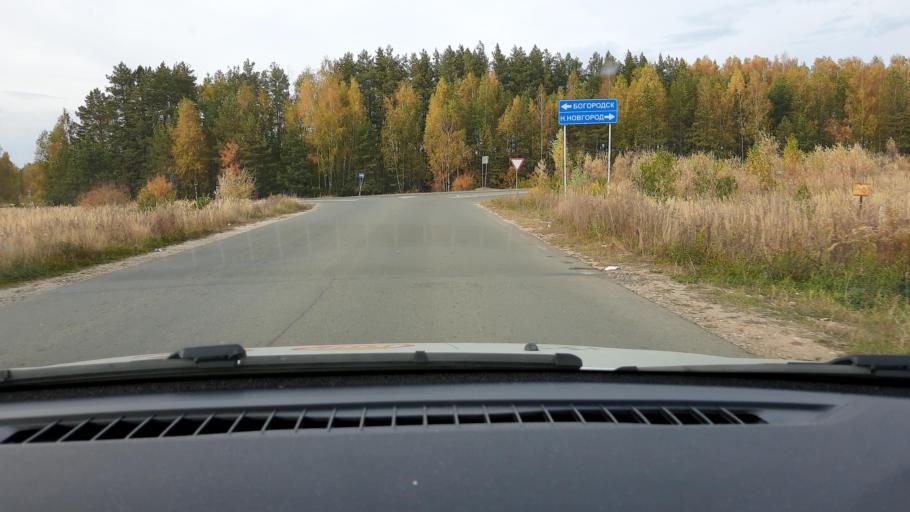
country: RU
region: Nizjnij Novgorod
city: Babino
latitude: 56.1365
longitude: 43.6425
